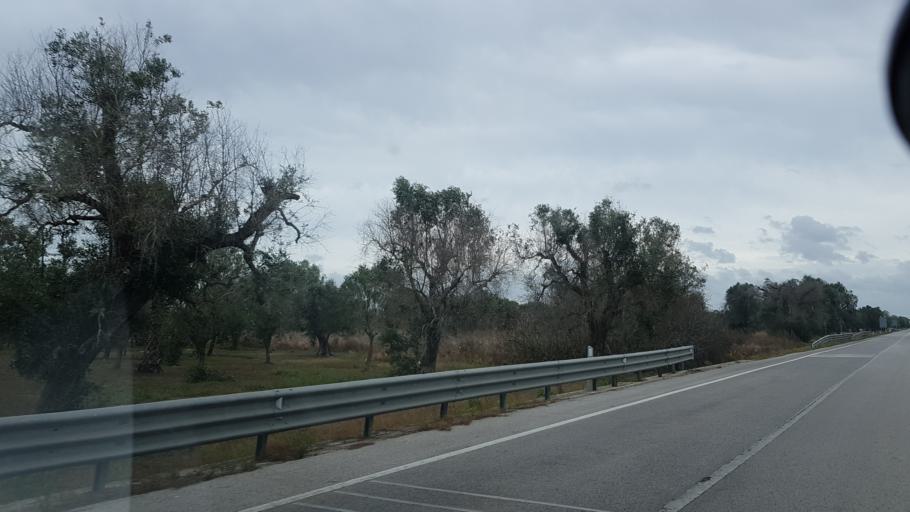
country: IT
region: Apulia
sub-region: Provincia di Lecce
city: Guagnano
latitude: 40.3984
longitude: 17.9237
